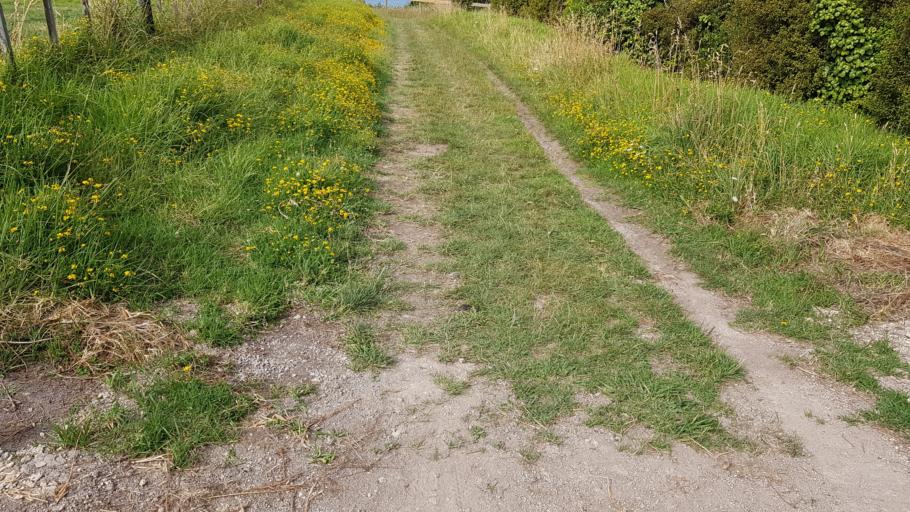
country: NZ
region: Auckland
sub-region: Auckland
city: Rothesay Bay
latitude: -36.6650
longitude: 174.7479
